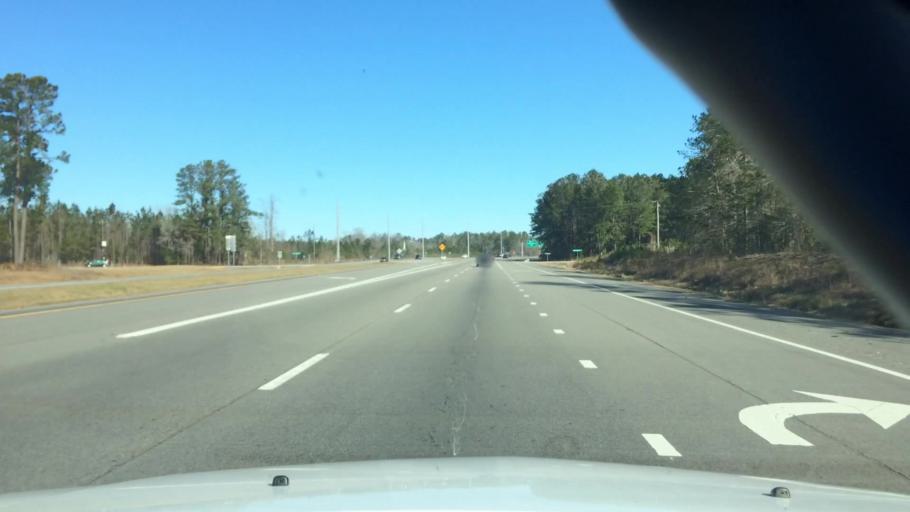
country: US
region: North Carolina
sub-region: Brunswick County
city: Leland
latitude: 34.1737
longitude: -78.0870
